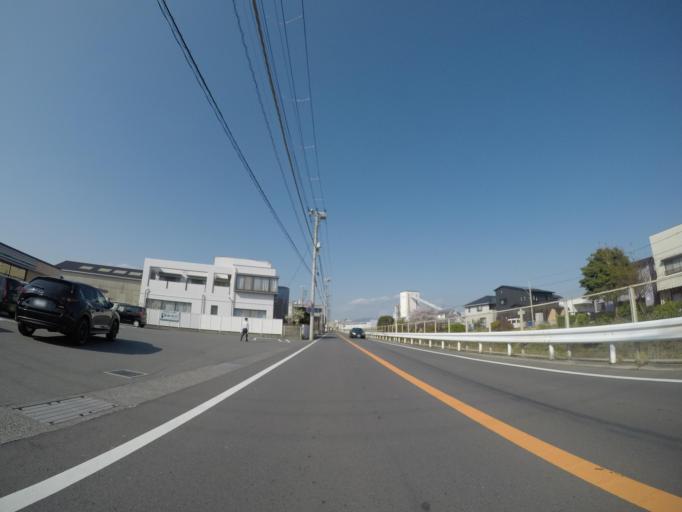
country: JP
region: Shizuoka
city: Numazu
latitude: 35.1036
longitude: 138.8469
